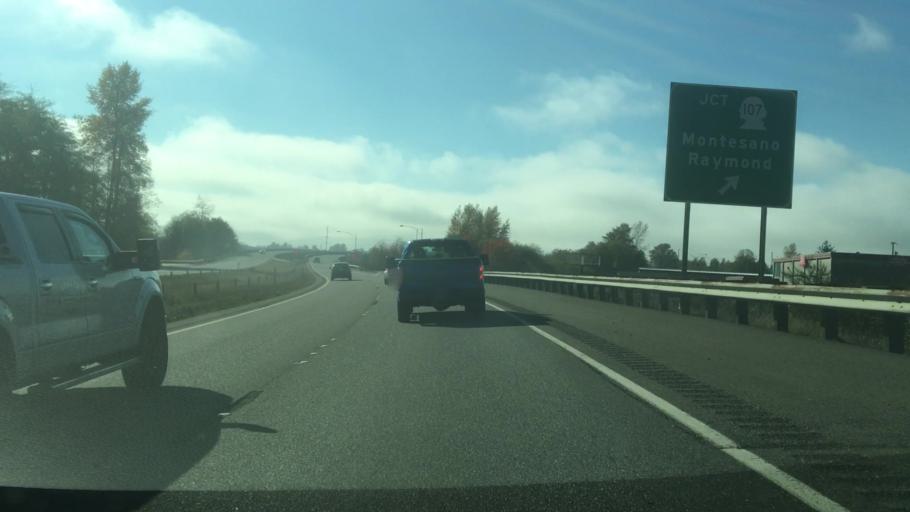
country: US
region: Washington
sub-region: Grays Harbor County
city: Montesano
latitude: 46.9782
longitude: -123.5947
